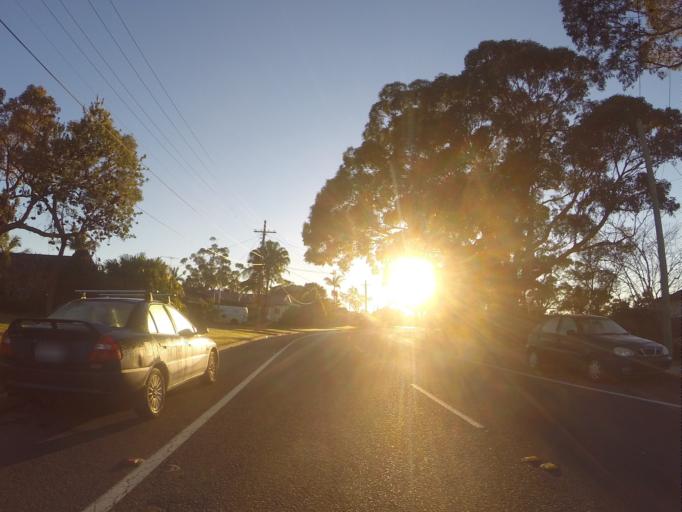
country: AU
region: New South Wales
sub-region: Sutherland Shire
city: Woronora Heights
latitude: -34.0452
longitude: 151.0169
